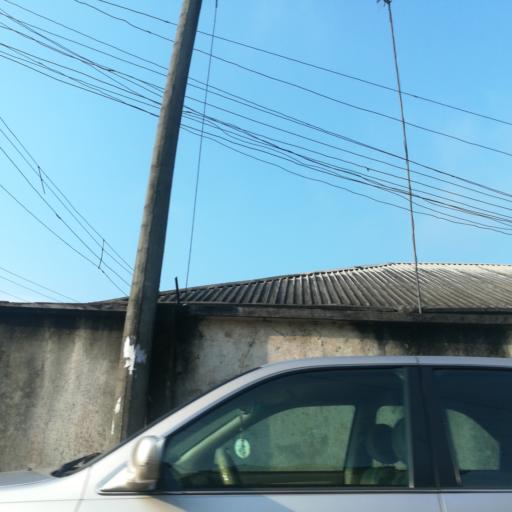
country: NG
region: Rivers
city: Port Harcourt
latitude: 4.8584
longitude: 6.9648
